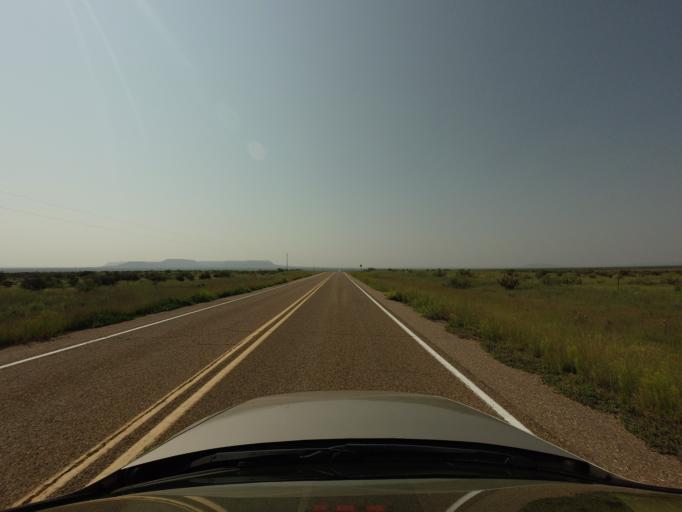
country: US
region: New Mexico
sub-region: Quay County
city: Tucumcari
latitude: 35.0710
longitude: -103.7376
